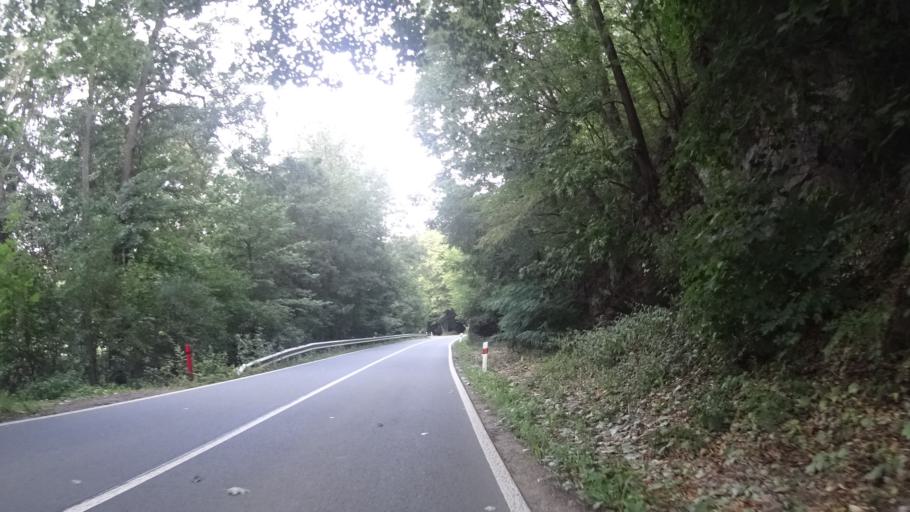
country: CZ
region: Olomoucky
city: Stity
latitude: 49.8683
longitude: 16.7329
